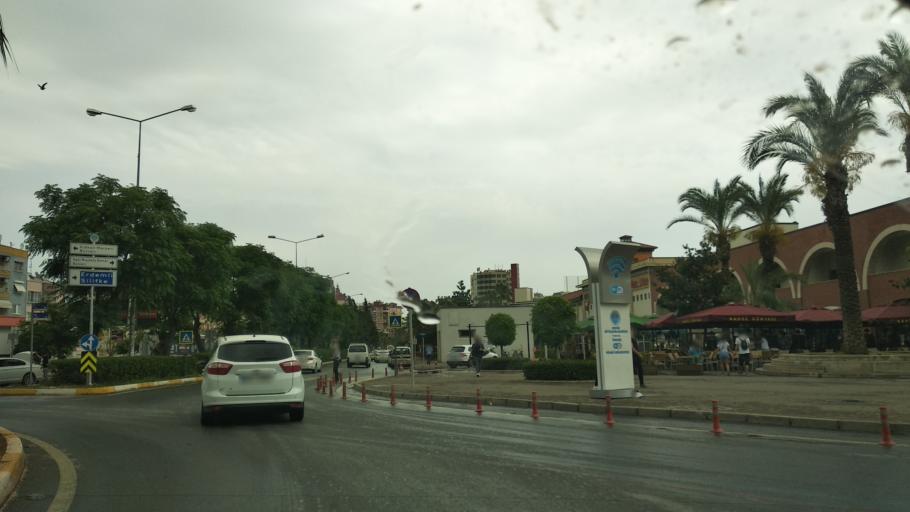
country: TR
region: Mersin
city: Mercin
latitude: 36.7846
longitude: 34.5894
